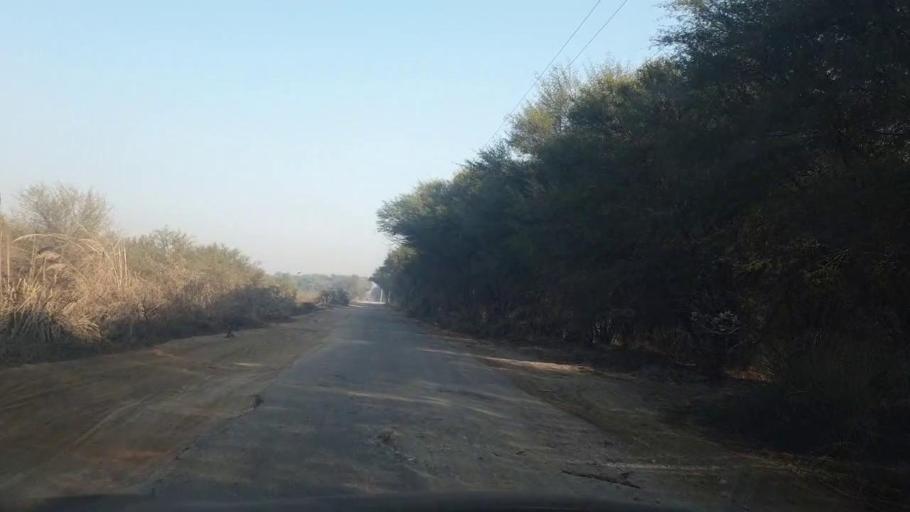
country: PK
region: Sindh
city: Mirpur Mathelo
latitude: 28.0529
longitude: 69.4615
